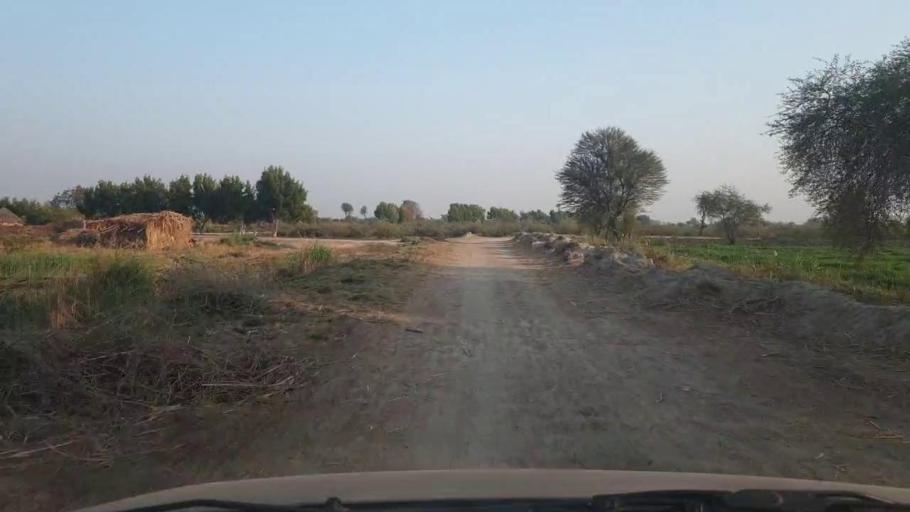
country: PK
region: Sindh
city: Mirwah Gorchani
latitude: 25.3612
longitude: 69.1526
